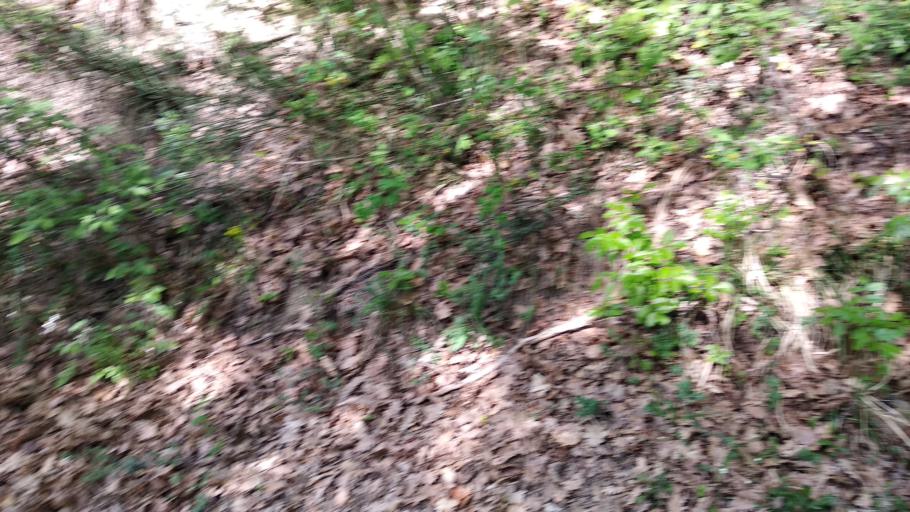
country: IT
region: Emilia-Romagna
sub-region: Provincia di Ravenna
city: Fognano
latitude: 44.2256
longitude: 11.7229
